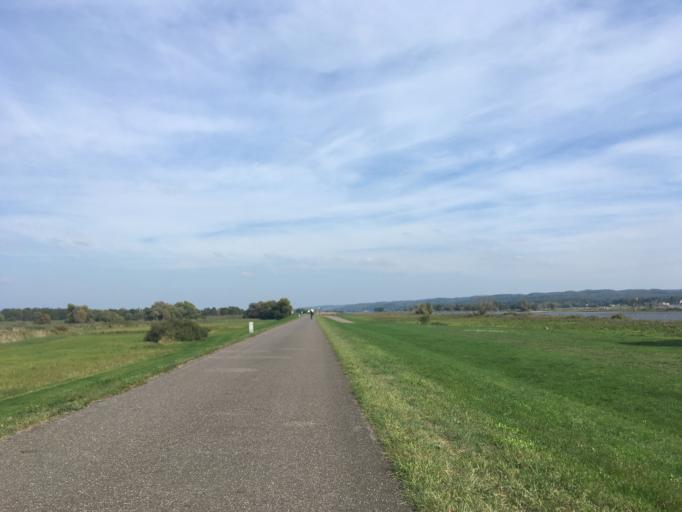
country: DE
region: Brandenburg
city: Schoneberg
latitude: 52.9785
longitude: 14.1800
